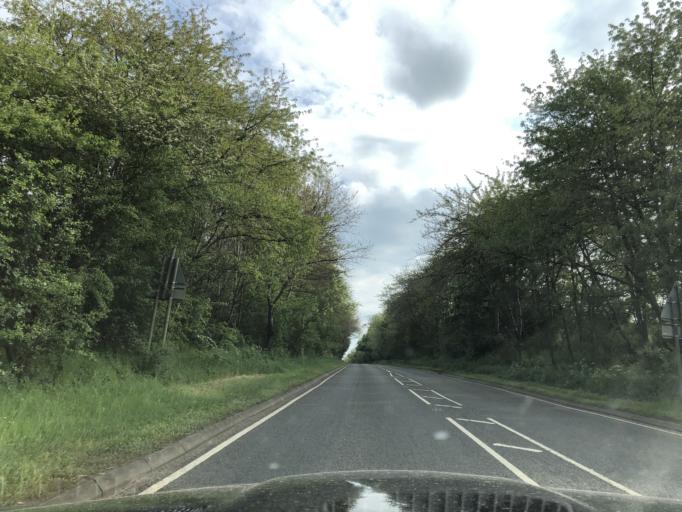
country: GB
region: England
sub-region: Warwickshire
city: Shipston on Stour
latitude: 52.1036
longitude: -1.6242
